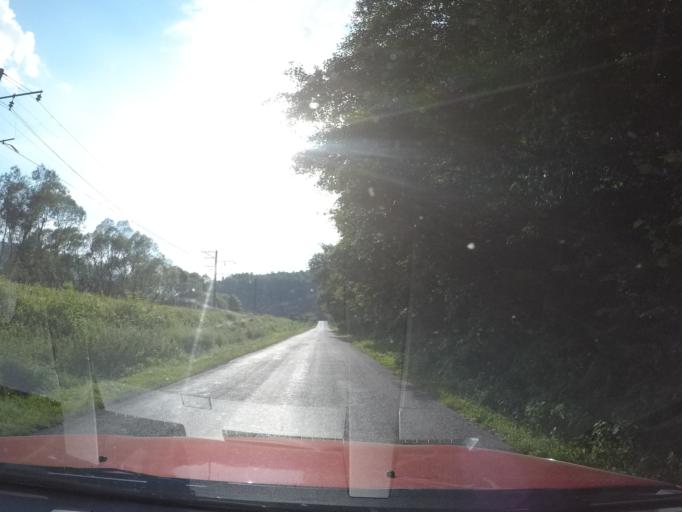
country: UA
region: Zakarpattia
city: Velykyi Bereznyi
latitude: 48.9528
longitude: 22.5513
